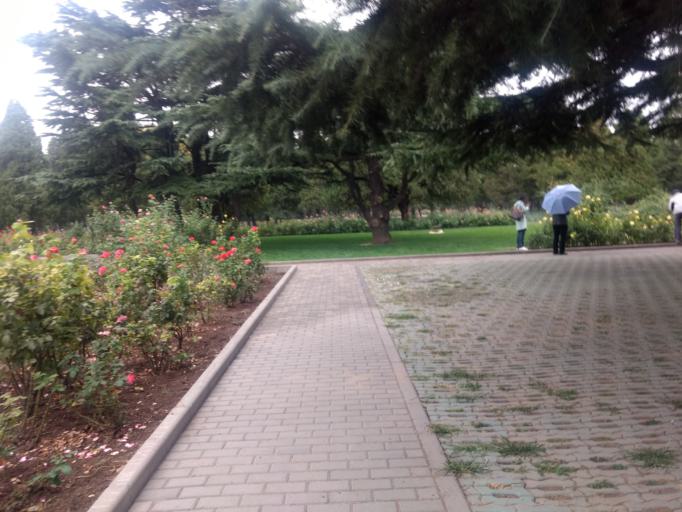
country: CN
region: Beijing
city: Longtan
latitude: 39.8813
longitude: 116.4034
